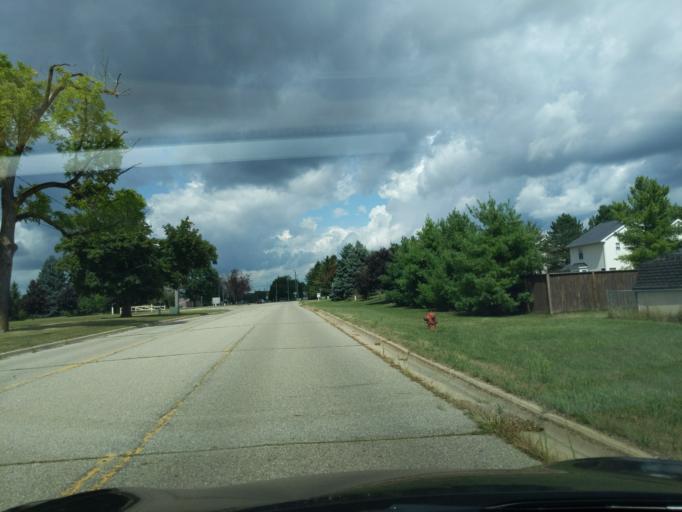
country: US
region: Michigan
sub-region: Ingham County
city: Holt
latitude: 42.6378
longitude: -84.5726
